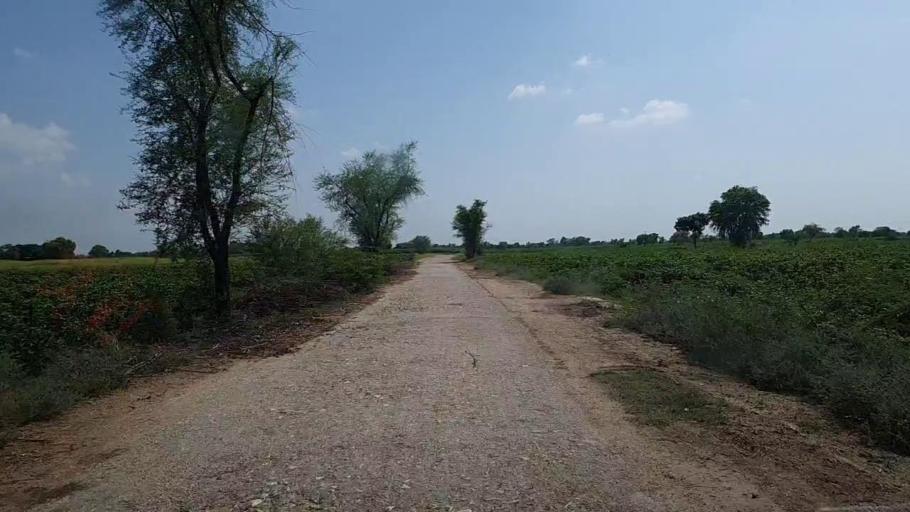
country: PK
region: Sindh
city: Kandiaro
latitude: 26.9995
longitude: 68.3064
